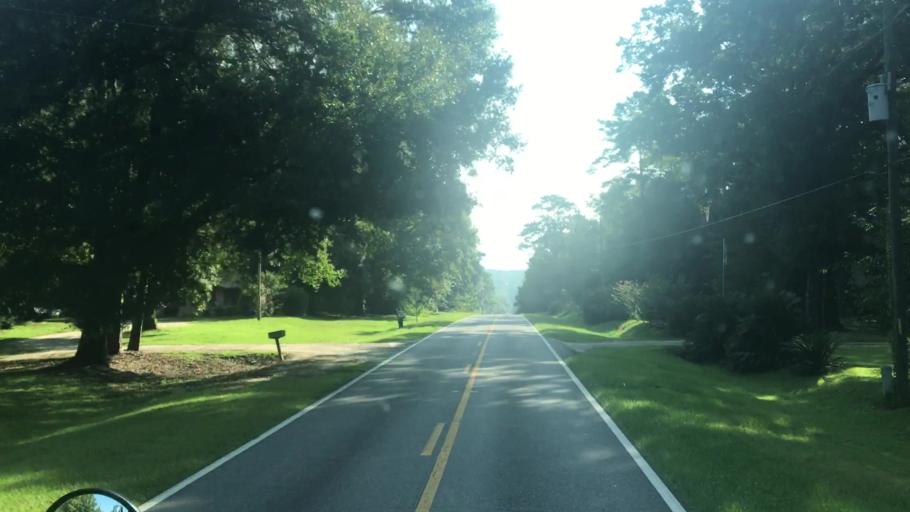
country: US
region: Florida
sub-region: Gadsden County
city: Quincy
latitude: 30.6625
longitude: -84.5586
